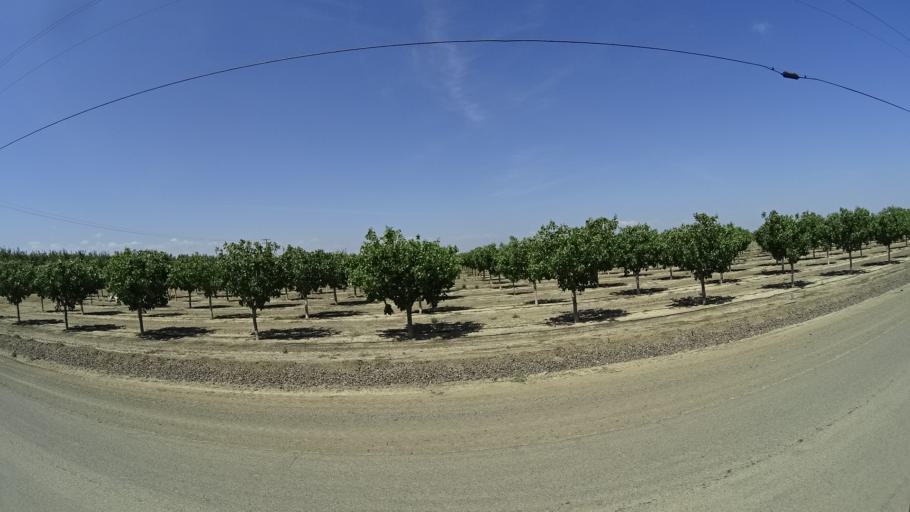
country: US
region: California
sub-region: Kings County
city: Kettleman City
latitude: 36.0946
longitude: -120.0037
